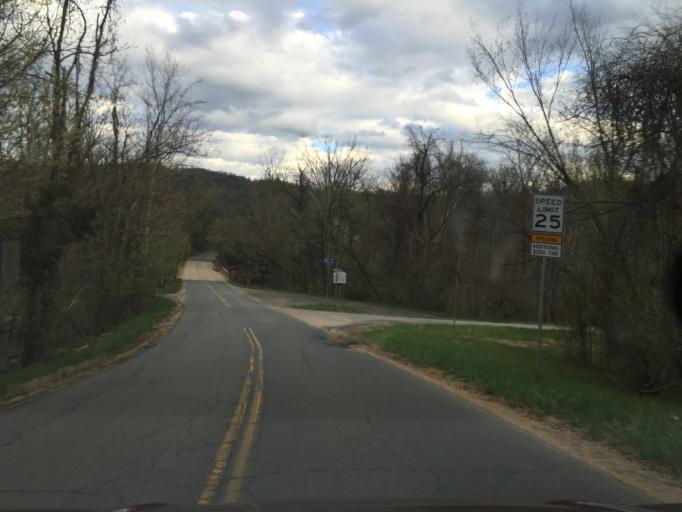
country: US
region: Maryland
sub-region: Frederick County
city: Point of Rocks
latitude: 39.2551
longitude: -77.5778
